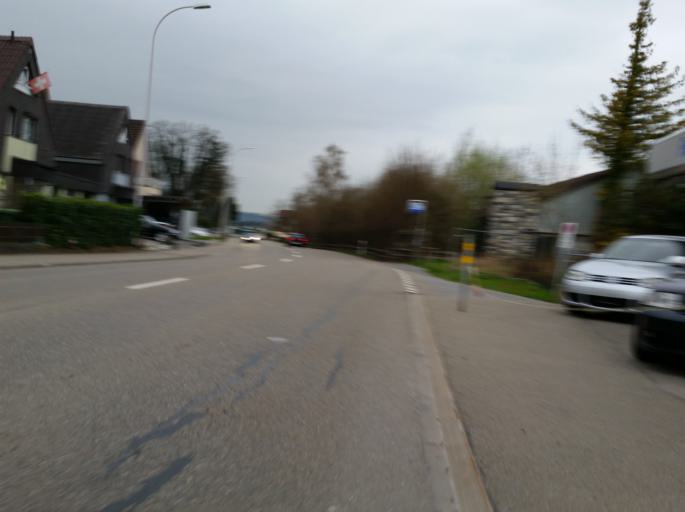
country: CH
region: Saint Gallen
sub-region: Wahlkreis Rheintal
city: Sankt Margrethen
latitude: 47.4551
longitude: 9.6247
